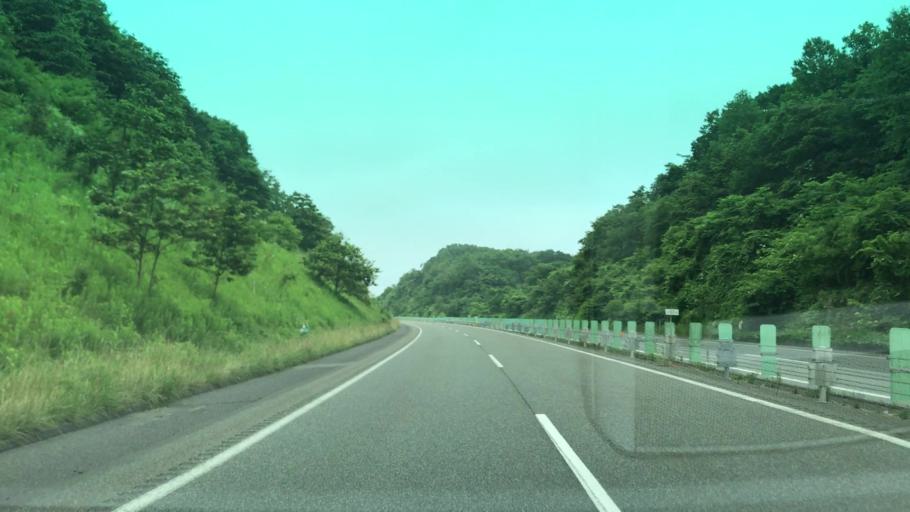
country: JP
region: Hokkaido
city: Shiraoi
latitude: 42.4871
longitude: 141.2320
